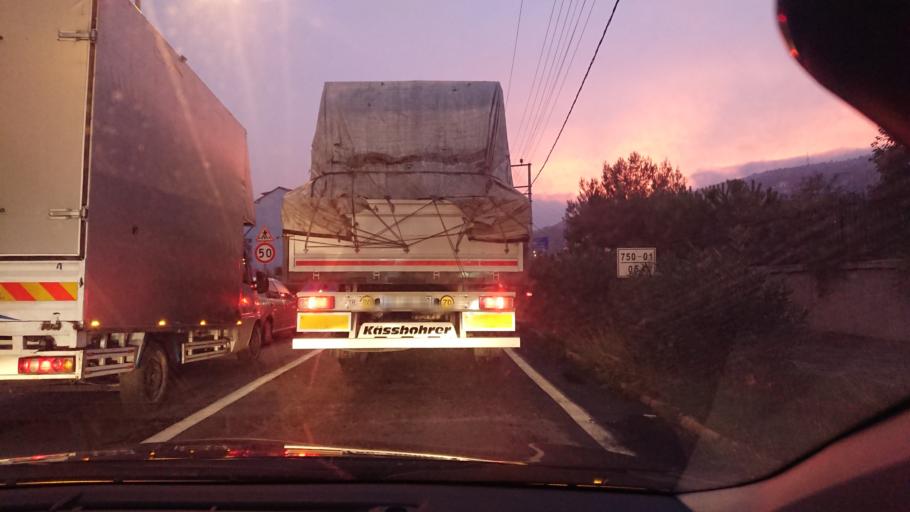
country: TR
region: Zonguldak
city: Devrek
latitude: 41.2265
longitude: 31.9647
